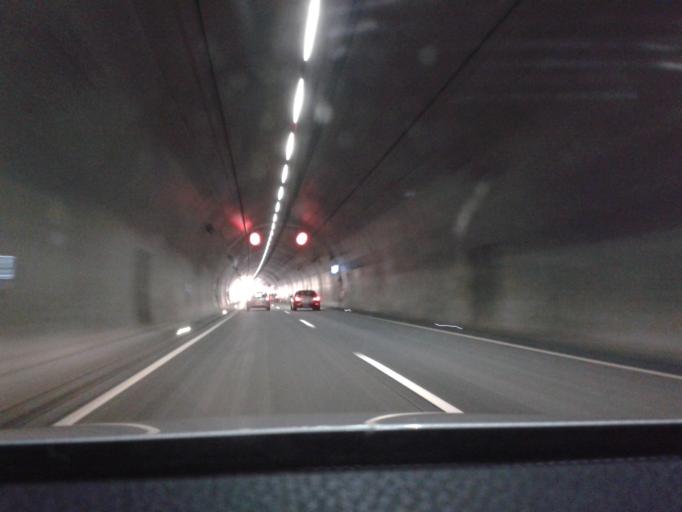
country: DE
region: Thuringia
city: Haynrode
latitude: 51.4118
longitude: 10.4696
